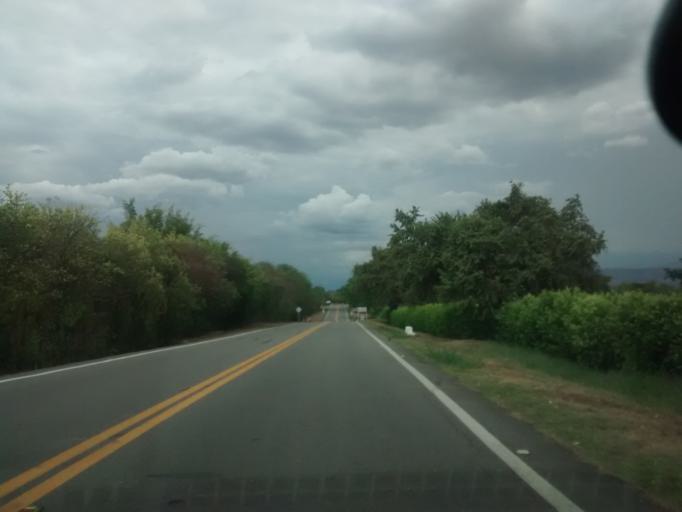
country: CO
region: Cundinamarca
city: Agua de Dios
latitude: 4.4082
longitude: -74.7182
